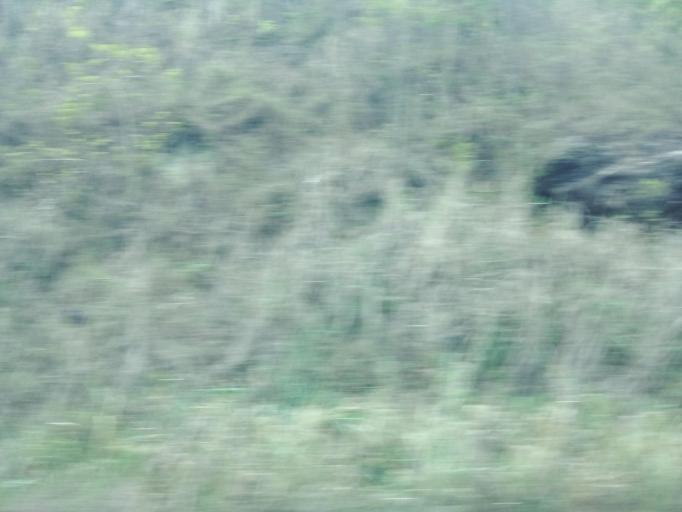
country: BR
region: Minas Gerais
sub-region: Joao Monlevade
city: Joao Monlevade
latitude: -19.8584
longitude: -43.1210
